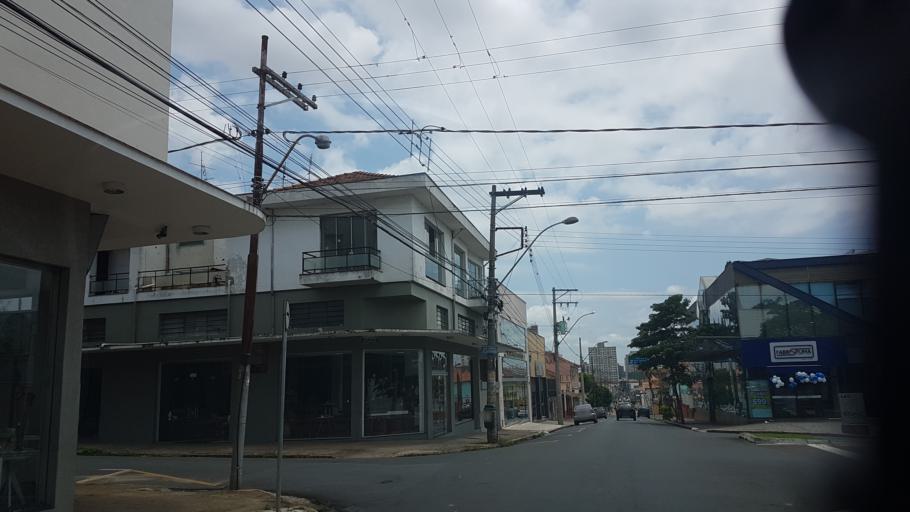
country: BR
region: Sao Paulo
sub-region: Piracicaba
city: Piracicaba
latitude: -22.7338
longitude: -47.6518
